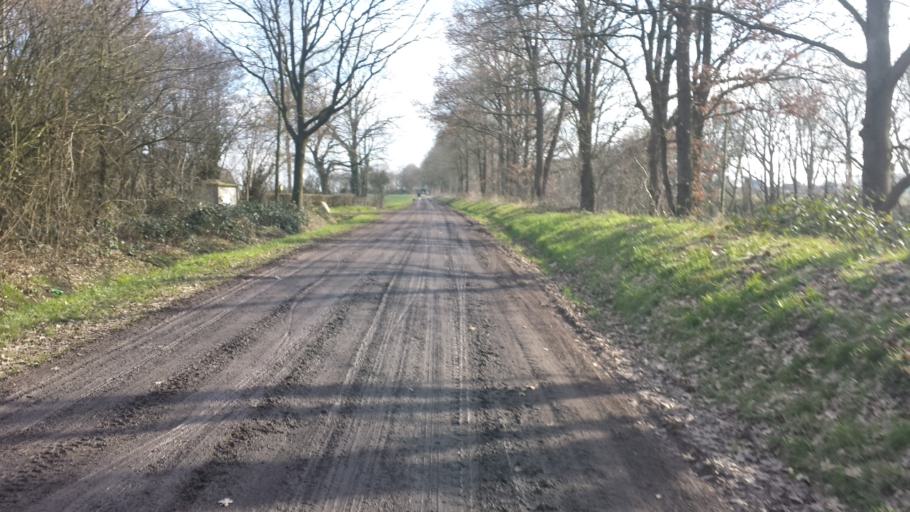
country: NL
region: Overijssel
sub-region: Gemeente Steenwijkerland
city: Tuk
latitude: 52.8082
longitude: 6.0870
